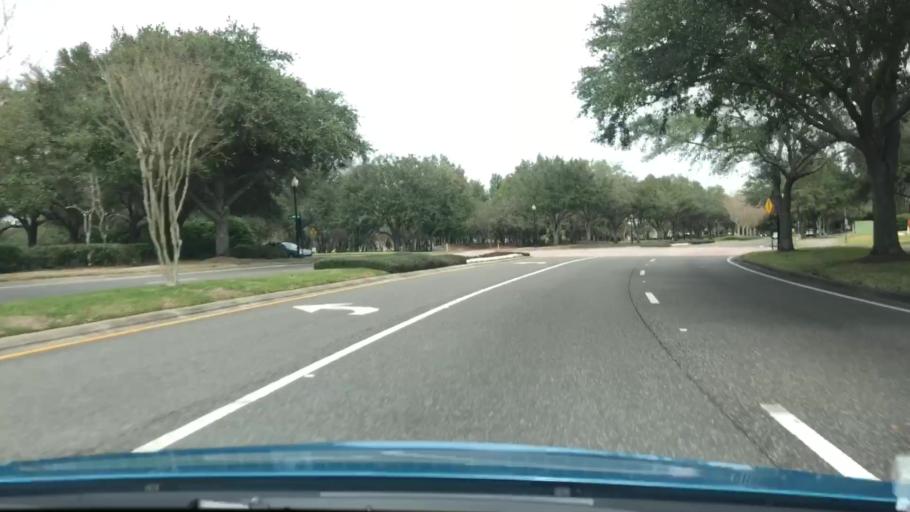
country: US
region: Florida
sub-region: Seminole County
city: Heathrow
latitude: 28.7755
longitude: -81.3588
